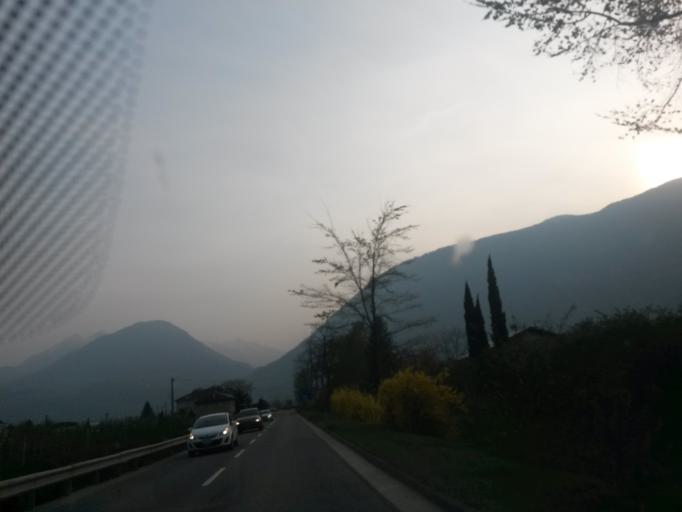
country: IT
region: Trentino-Alto Adige
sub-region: Bolzano
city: Sinigo
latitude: 46.6499
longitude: 11.1796
